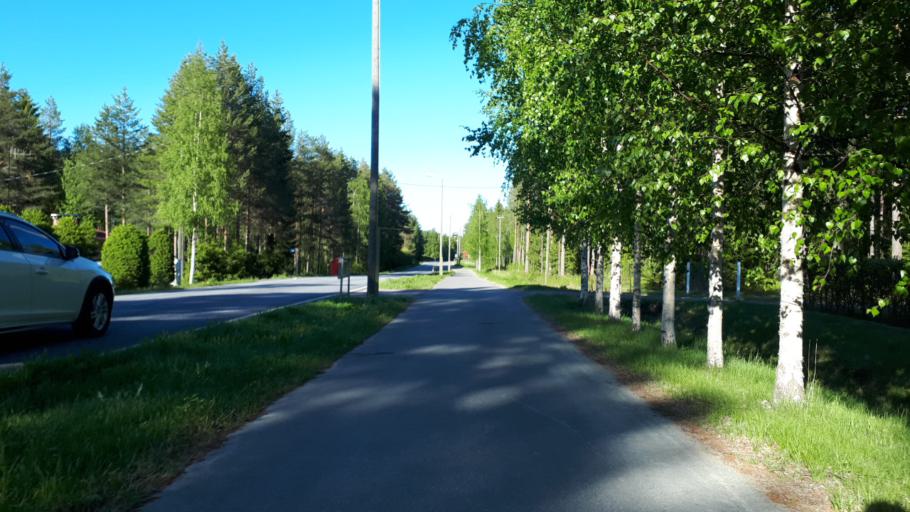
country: FI
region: Northern Ostrobothnia
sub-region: Oulunkaari
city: Ii
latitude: 65.3234
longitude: 25.4708
